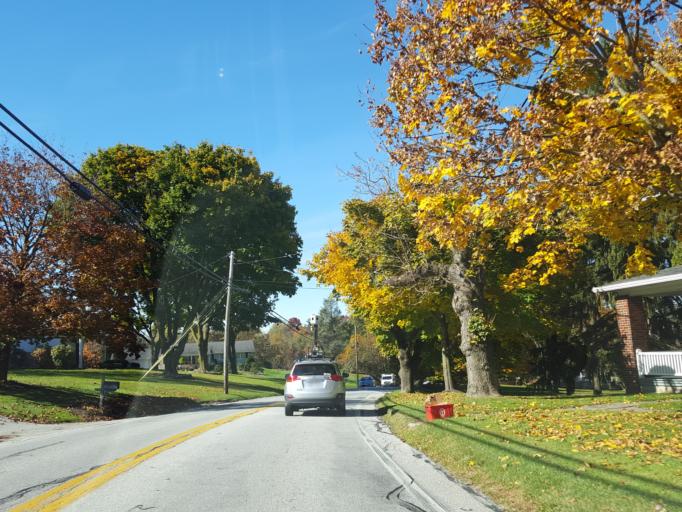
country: US
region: Pennsylvania
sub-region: York County
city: Spry
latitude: 39.9306
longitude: -76.6670
